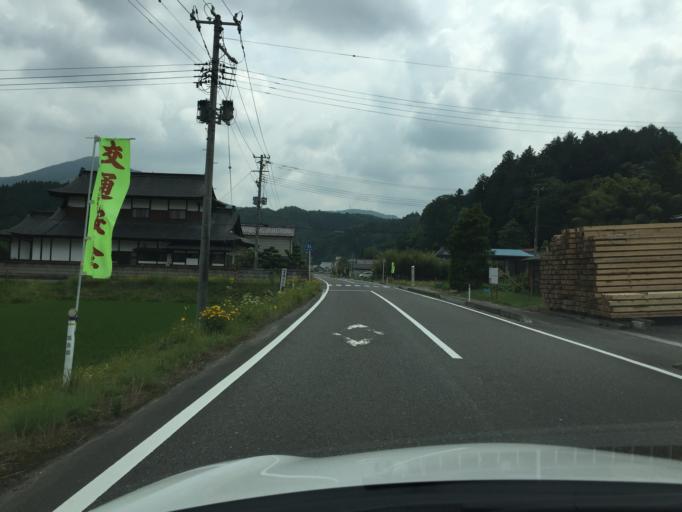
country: JP
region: Fukushima
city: Miharu
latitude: 37.2959
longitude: 140.5400
